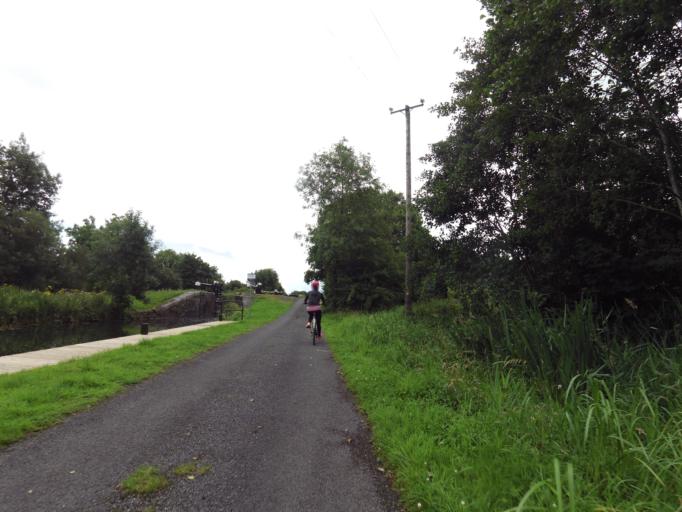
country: IE
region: Leinster
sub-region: An Iarmhi
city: An Muileann gCearr
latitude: 53.5375
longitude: -7.4735
